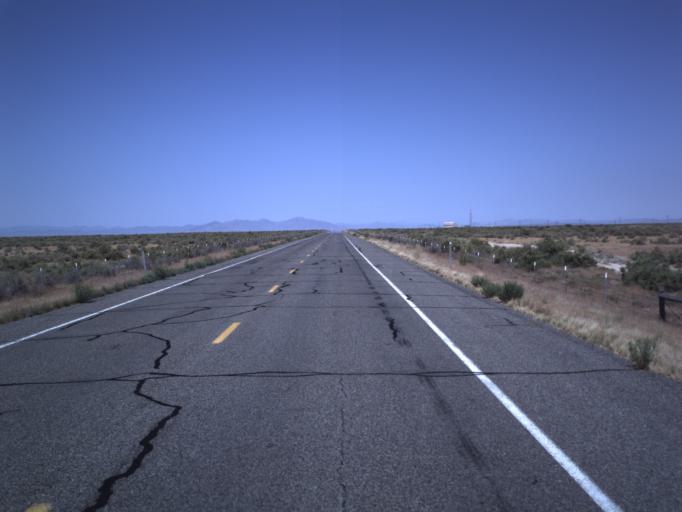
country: US
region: Utah
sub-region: Millard County
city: Delta
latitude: 39.4689
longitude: -112.4538
